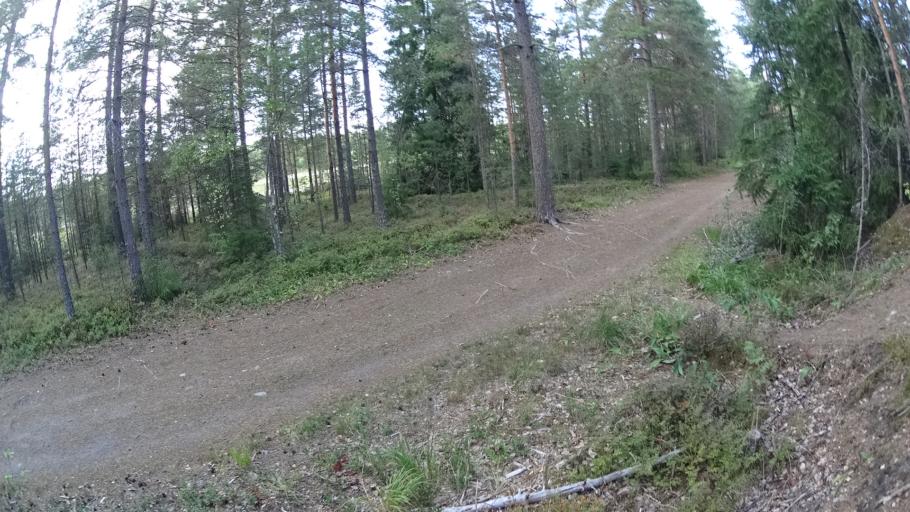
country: FI
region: Uusimaa
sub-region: Helsinki
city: Vihti
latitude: 60.3270
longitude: 24.2856
